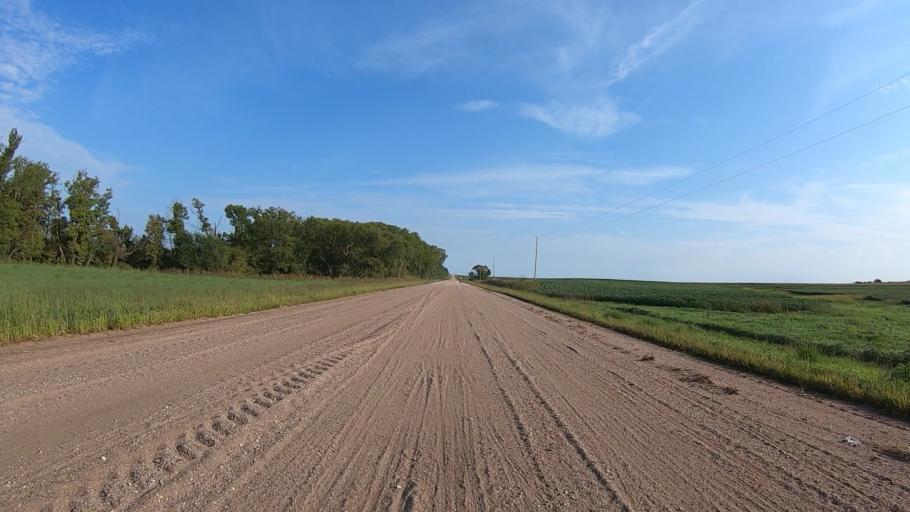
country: US
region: Kansas
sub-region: Marshall County
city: Blue Rapids
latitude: 39.6540
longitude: -96.8628
